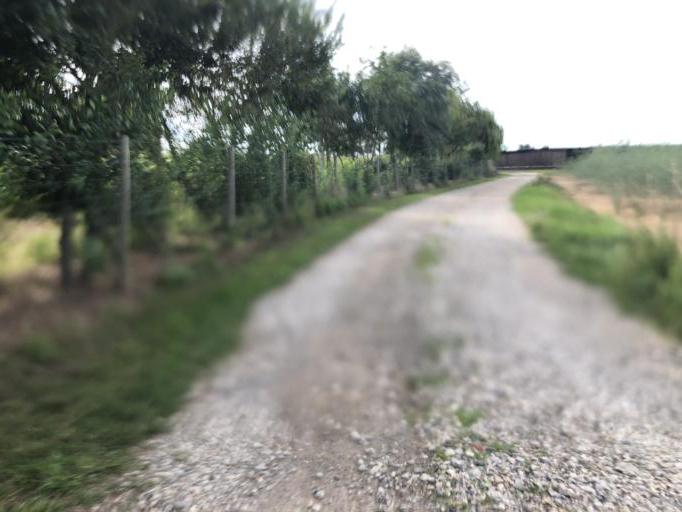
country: DE
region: Bavaria
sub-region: Regierungsbezirk Mittelfranken
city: Furth
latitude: 49.5267
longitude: 11.0012
